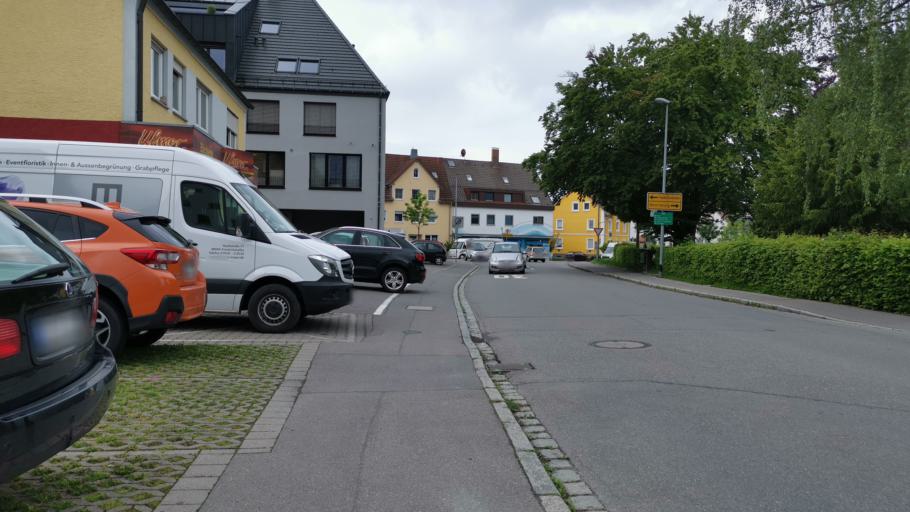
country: DE
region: Baden-Wuerttemberg
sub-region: Tuebingen Region
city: Immenstaad am Bodensee
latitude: 47.6709
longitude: 9.4128
